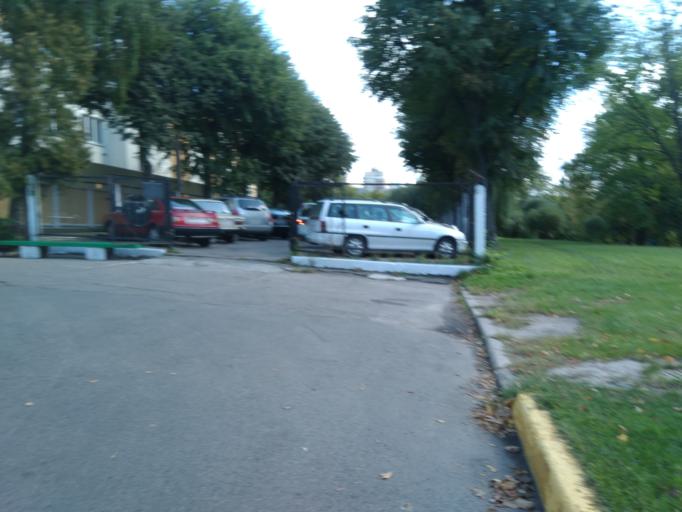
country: BY
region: Minsk
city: Minsk
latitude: 53.8917
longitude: 27.5806
